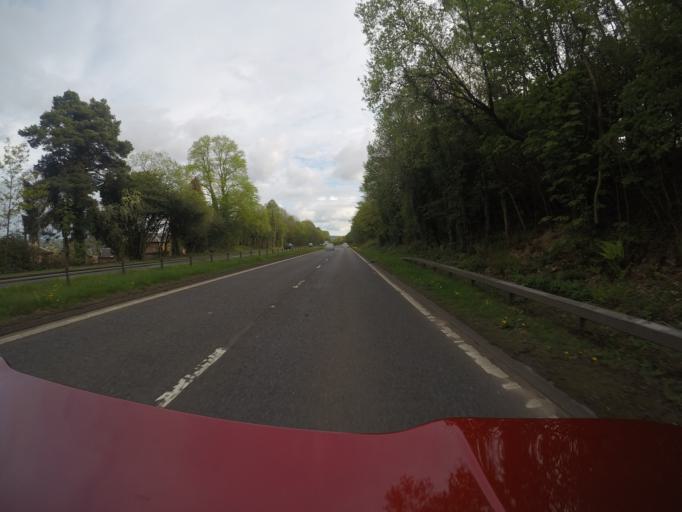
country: GB
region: Scotland
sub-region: West Dunbartonshire
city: Renton
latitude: 55.9689
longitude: -4.5877
